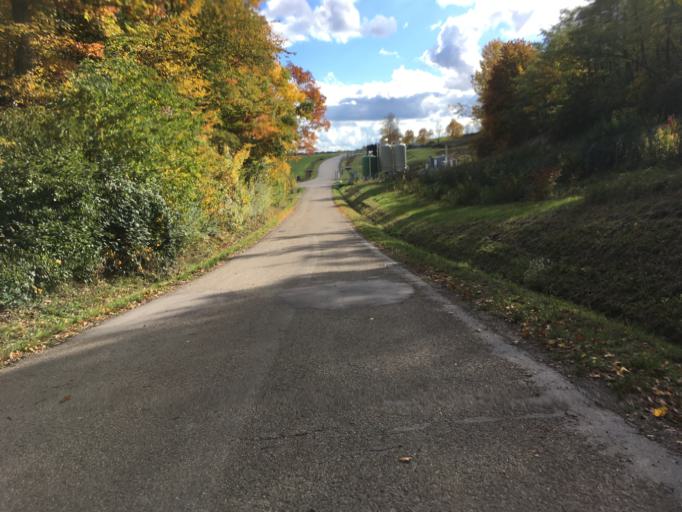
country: DE
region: Baden-Wuerttemberg
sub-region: Regierungsbezirk Stuttgart
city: Waldenburg
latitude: 49.1840
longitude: 9.6754
